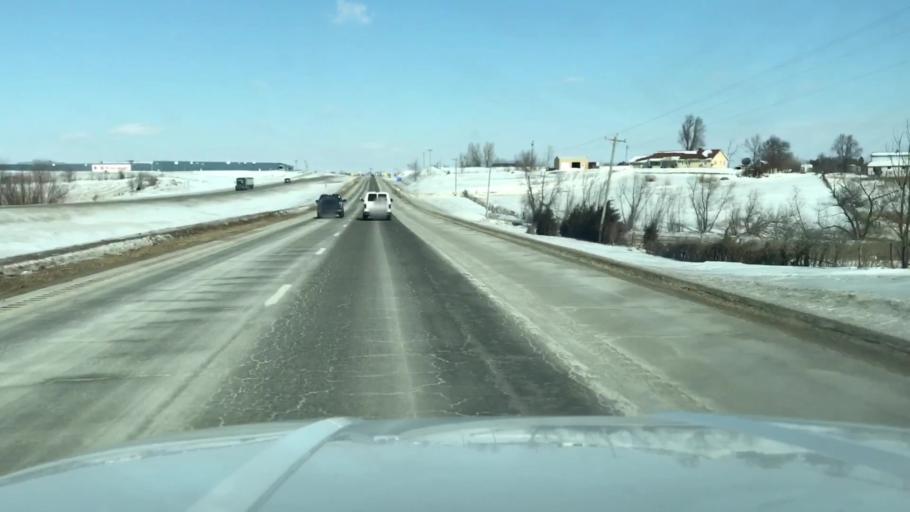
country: US
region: Missouri
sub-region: Nodaway County
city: Maryville
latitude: 40.3032
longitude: -94.8745
